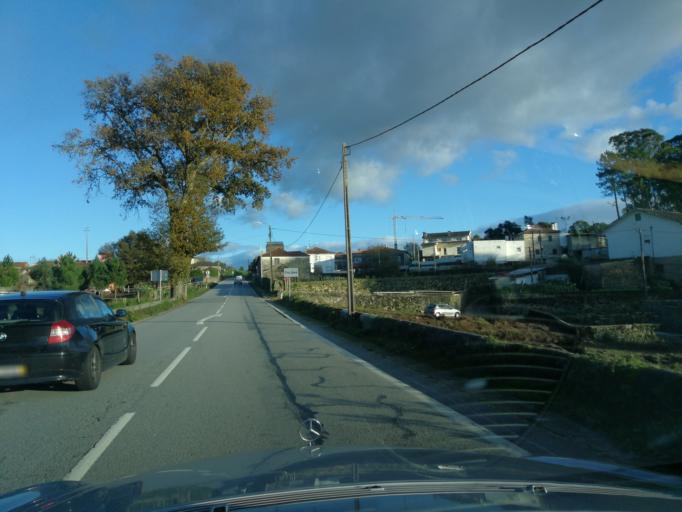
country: PT
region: Braga
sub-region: Esposende
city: Marinhas
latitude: 41.6161
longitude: -8.7514
